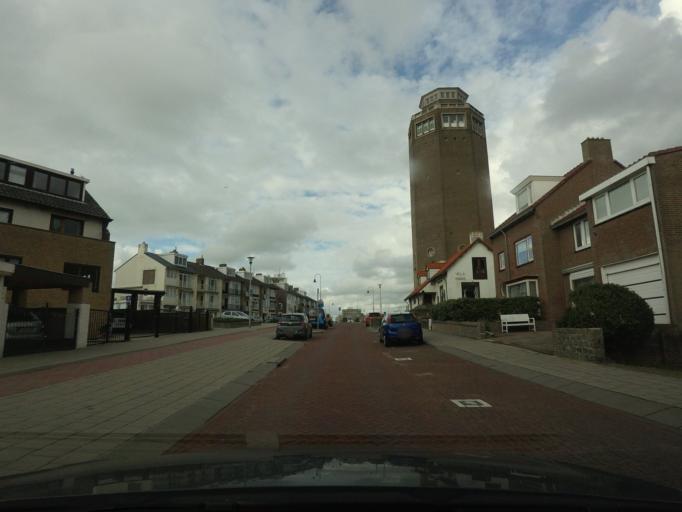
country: NL
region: North Holland
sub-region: Gemeente Zandvoort
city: Zandvoort
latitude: 52.3699
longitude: 4.5243
